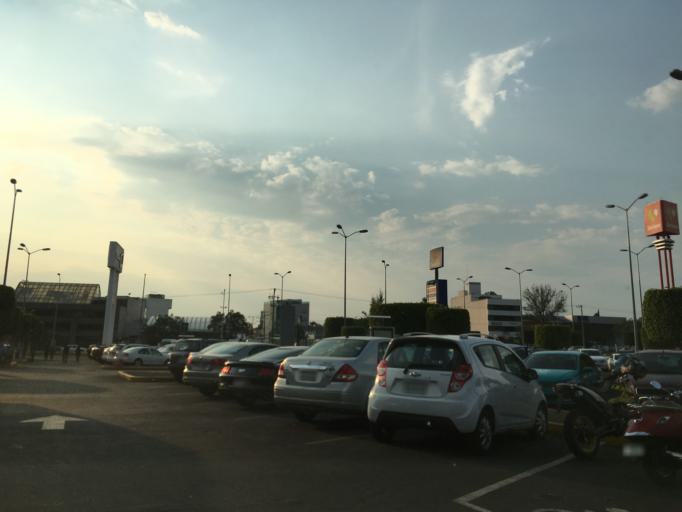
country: MX
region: Michoacan
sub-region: Morelia
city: Puerto de Buenavista (Lazaro Cardenas)
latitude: 19.6876
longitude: -101.1514
